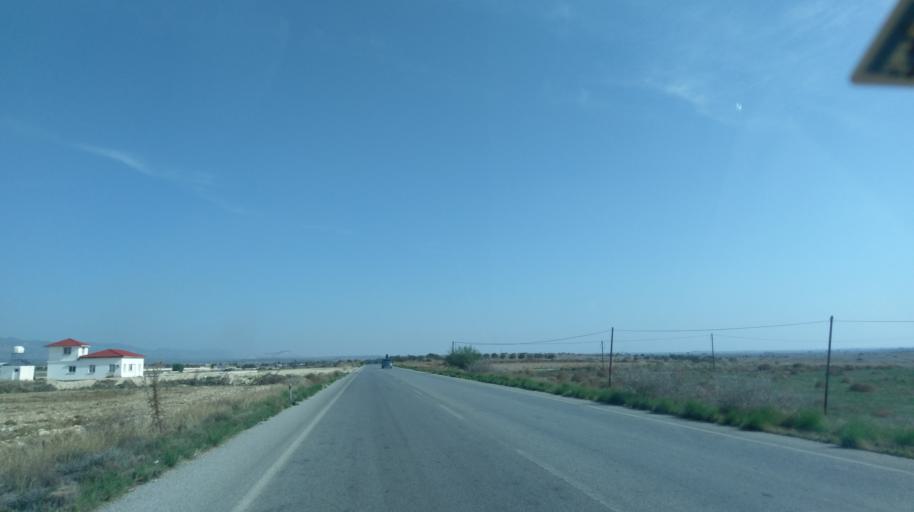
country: CY
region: Ammochostos
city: Lefkonoiko
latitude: 35.2559
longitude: 33.6359
